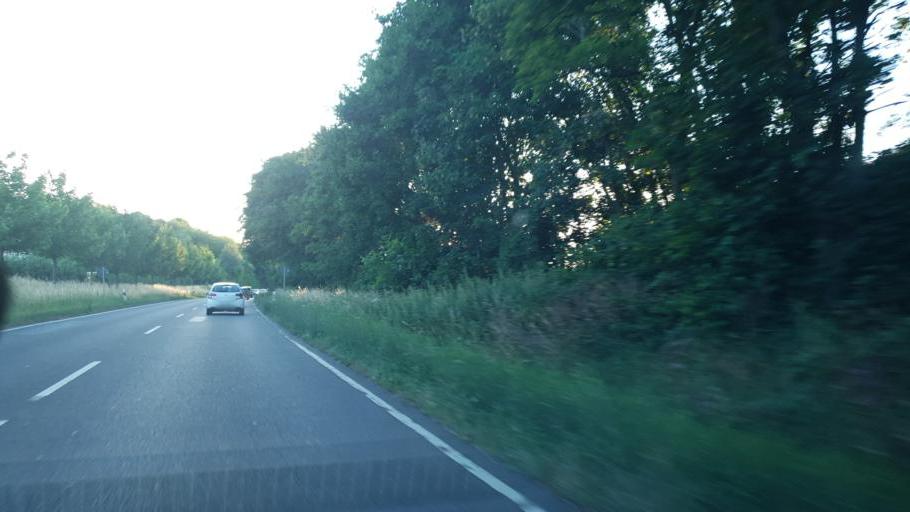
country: DE
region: Hesse
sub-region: Regierungsbezirk Darmstadt
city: Kriftel
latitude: 50.0790
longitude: 8.4619
